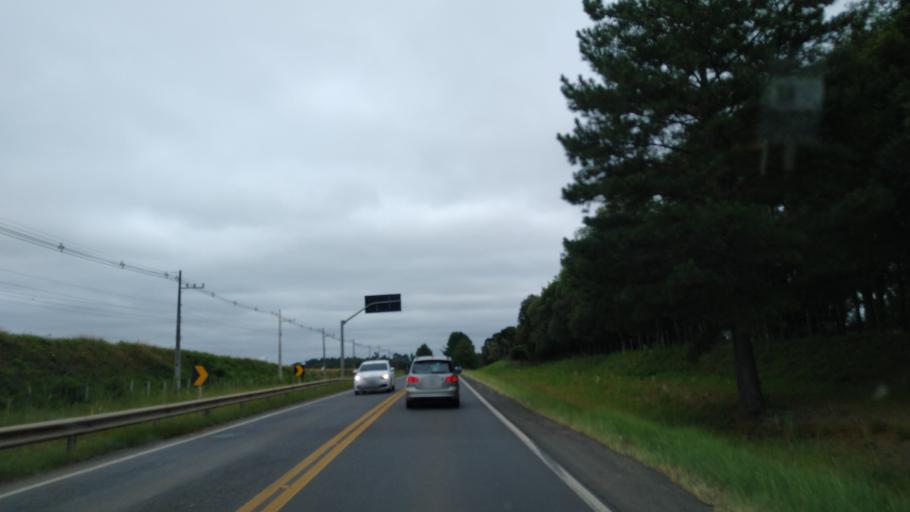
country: BR
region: Santa Catarina
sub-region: Canoinhas
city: Canoinhas
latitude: -26.2328
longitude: -50.4677
